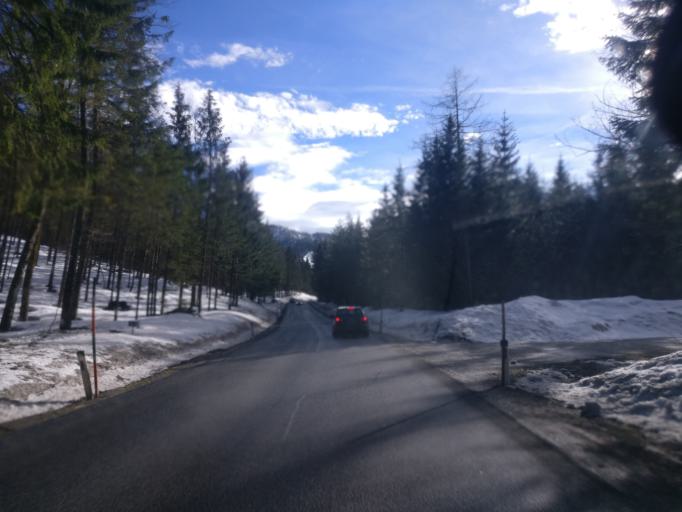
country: AT
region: Styria
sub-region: Politischer Bezirk Liezen
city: Sankt Gallen
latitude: 47.6291
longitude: 14.5581
